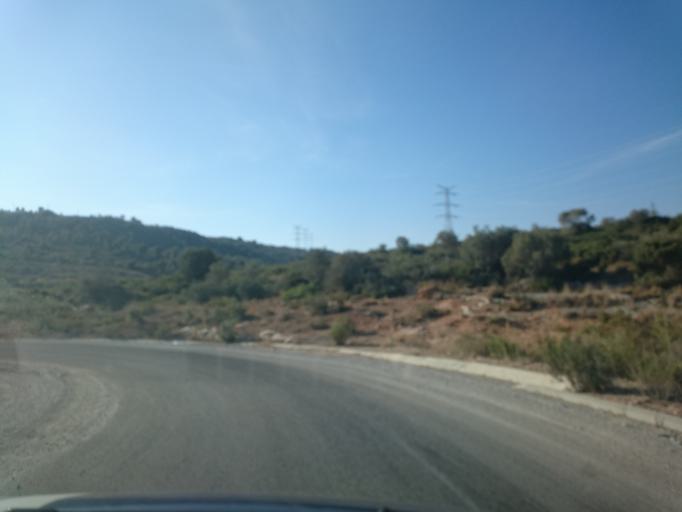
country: ES
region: Catalonia
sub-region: Provincia de Barcelona
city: Vilanova i la Geltru
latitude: 41.2549
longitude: 1.7177
